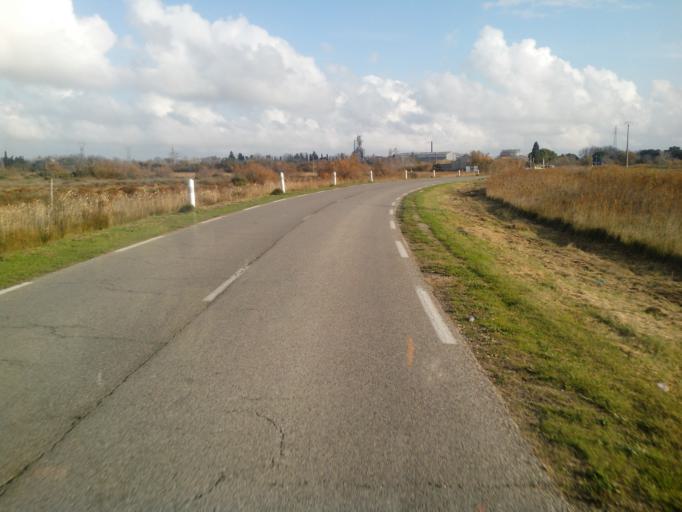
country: FR
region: Provence-Alpes-Cote d'Azur
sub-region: Departement des Bouches-du-Rhone
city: Port-Saint-Louis-du-Rhone
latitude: 43.4227
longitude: 4.7278
